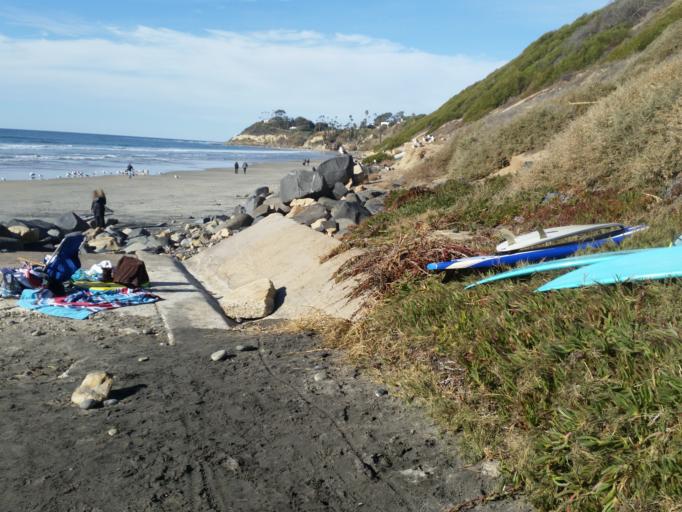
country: US
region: California
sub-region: San Diego County
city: Encinitas
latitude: 33.0282
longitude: -117.2884
